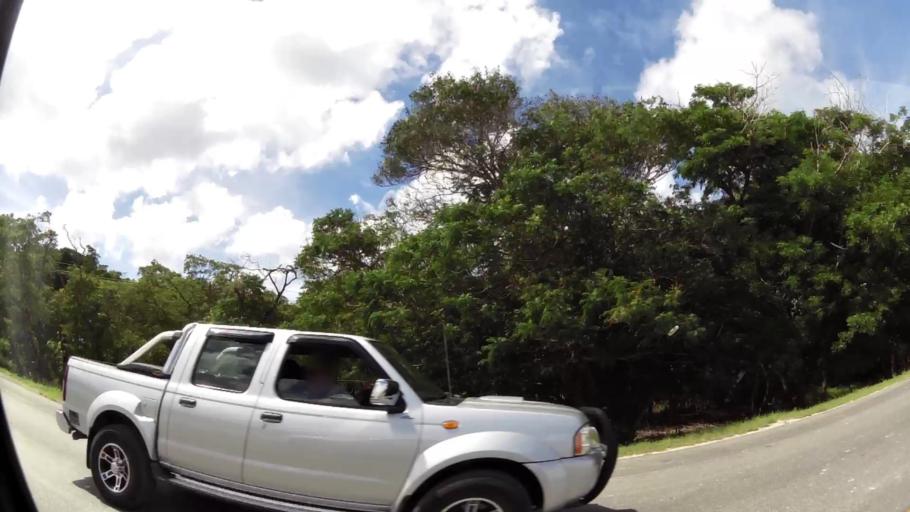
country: BB
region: Saint Michael
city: Bridgetown
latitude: 13.1173
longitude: -59.6269
